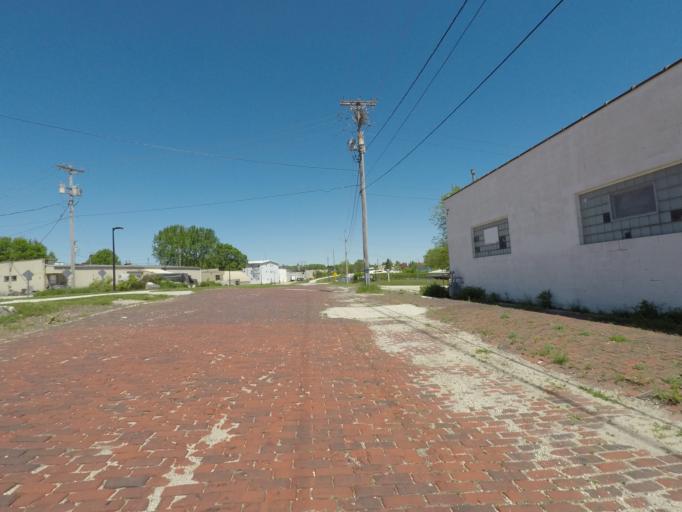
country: US
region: Wisconsin
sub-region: Sheboygan County
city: Sheboygan
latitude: 43.7519
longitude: -87.7202
